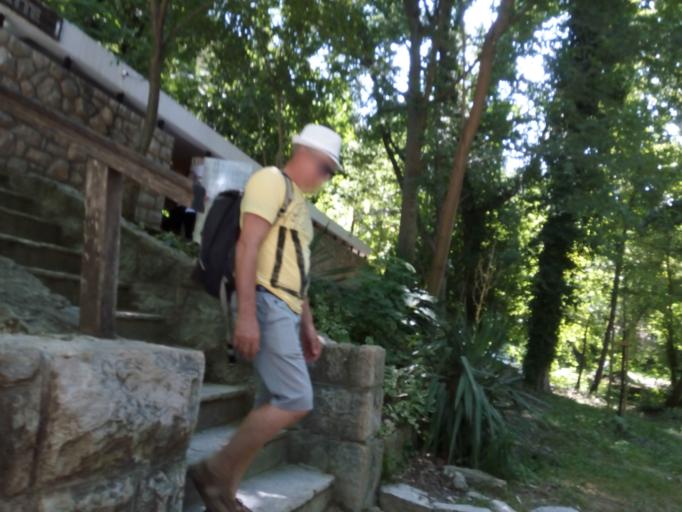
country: HR
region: Sibensko-Kniniska
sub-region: Grad Sibenik
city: Sibenik
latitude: 43.8074
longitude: 15.9632
